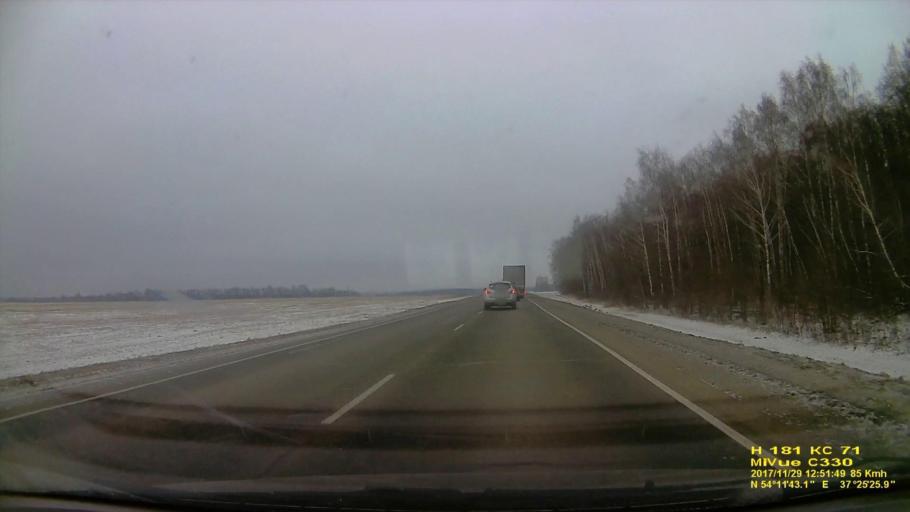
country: RU
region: Tula
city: Barsuki
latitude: 54.1954
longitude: 37.4237
